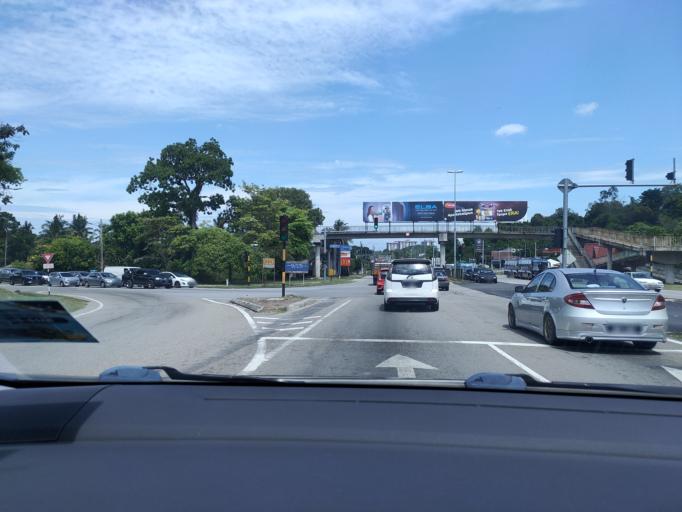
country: MY
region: Melaka
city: Batu Berendam
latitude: 2.2596
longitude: 102.2217
